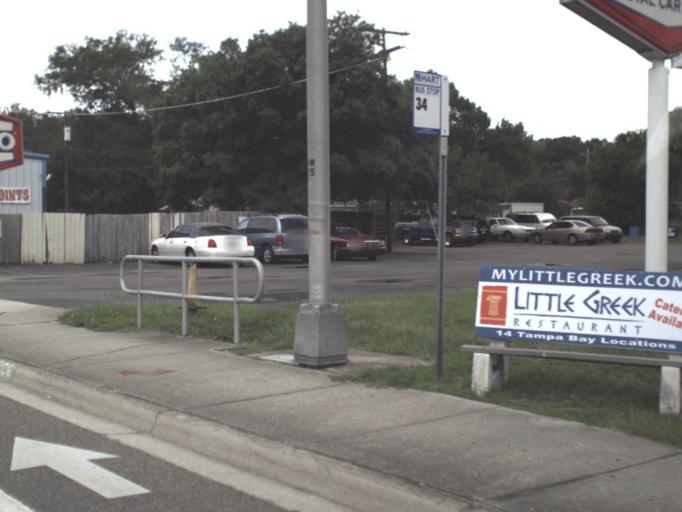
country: US
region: Florida
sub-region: Hillsborough County
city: Egypt Lake-Leto
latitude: 27.9963
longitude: -82.4907
